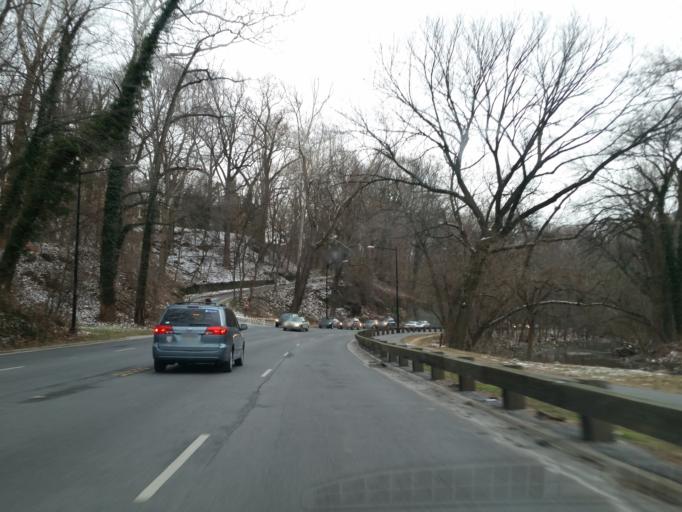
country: US
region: Washington, D.C.
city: Washington, D.C.
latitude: 38.9194
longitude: -77.0547
